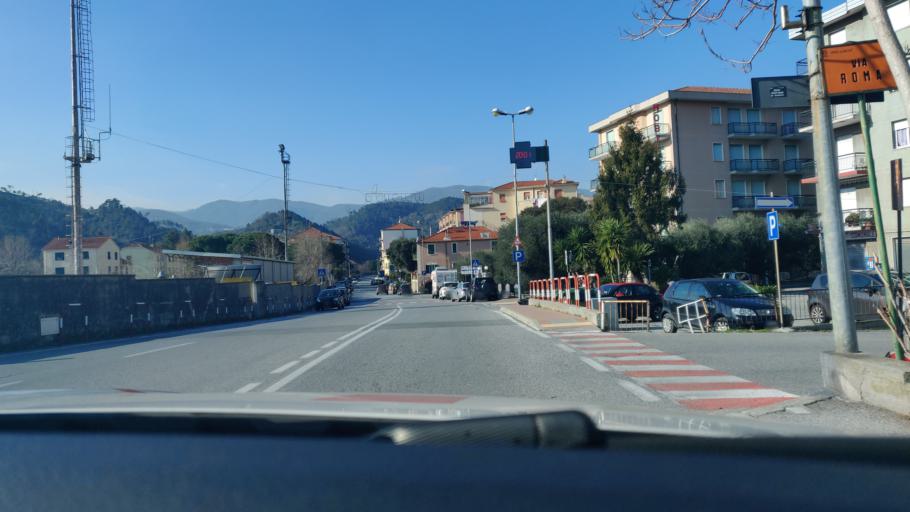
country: IT
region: Liguria
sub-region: Provincia di Savona
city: Quiliano
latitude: 44.2916
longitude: 8.4171
